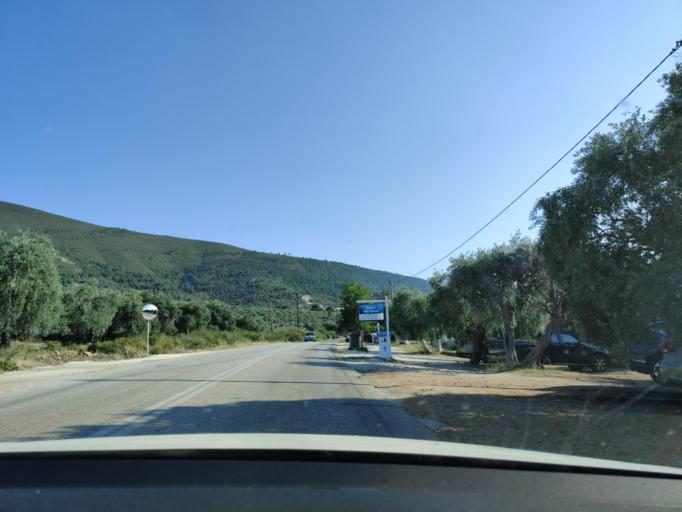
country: GR
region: East Macedonia and Thrace
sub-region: Nomos Kavalas
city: Prinos
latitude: 40.6881
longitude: 24.5267
